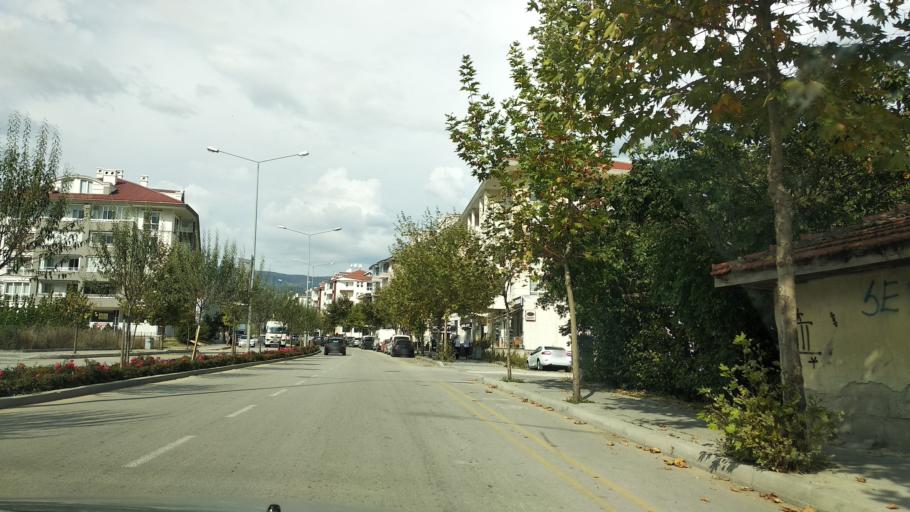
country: TR
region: Bolu
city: Bolu
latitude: 40.7310
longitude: 31.5890
